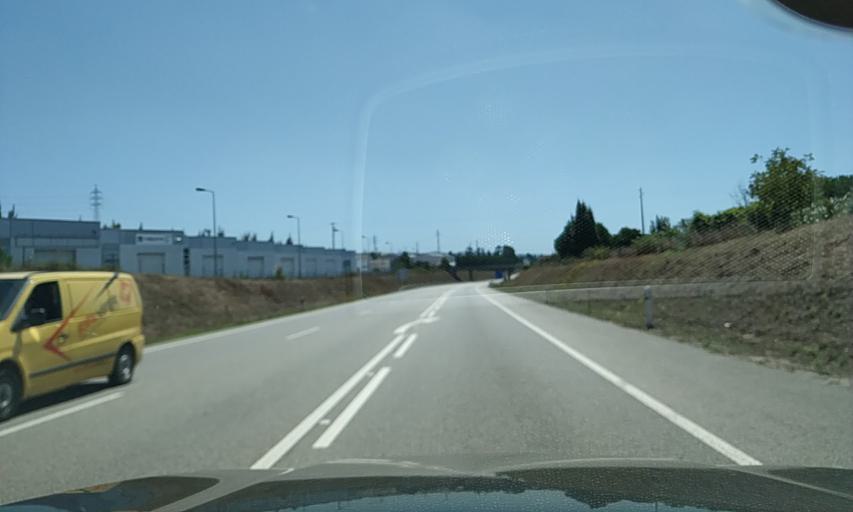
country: PT
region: Aveiro
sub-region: Agueda
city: Aguada de Cima
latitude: 40.5382
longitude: -8.4624
